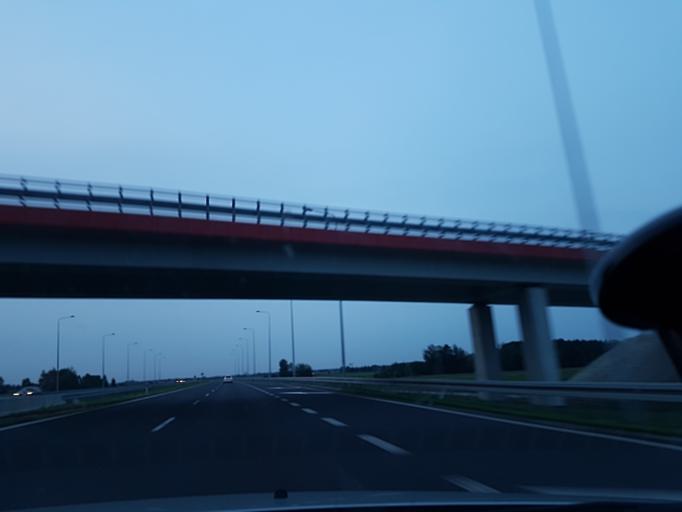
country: PL
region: Lodz Voivodeship
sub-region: Powiat leczycki
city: Piatek
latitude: 52.0032
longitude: 19.5446
